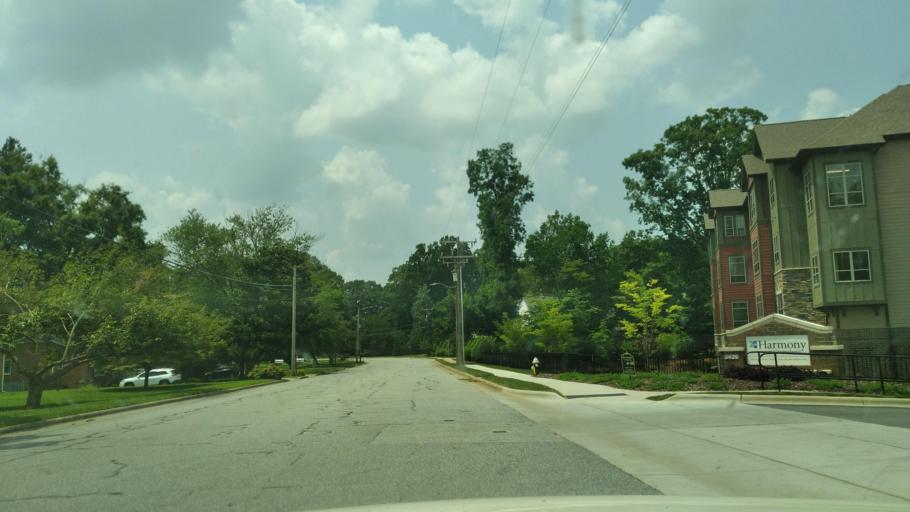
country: US
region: North Carolina
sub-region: Guilford County
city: Greensboro
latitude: 36.1198
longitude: -79.8476
